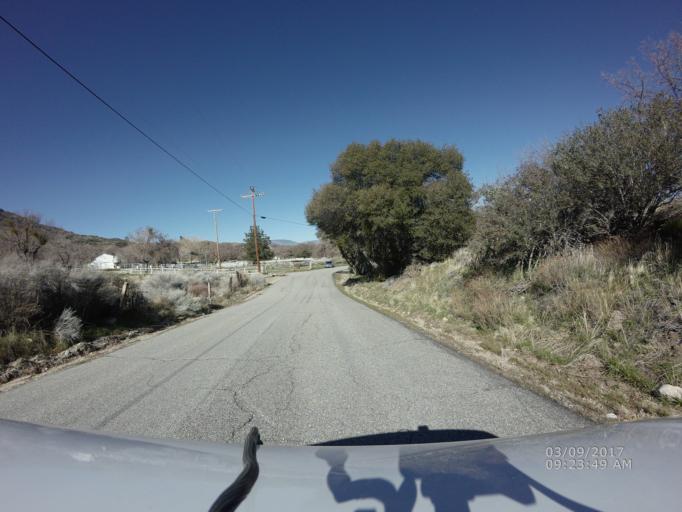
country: US
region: California
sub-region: Kern County
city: Lebec
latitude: 34.7462
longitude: -118.6785
